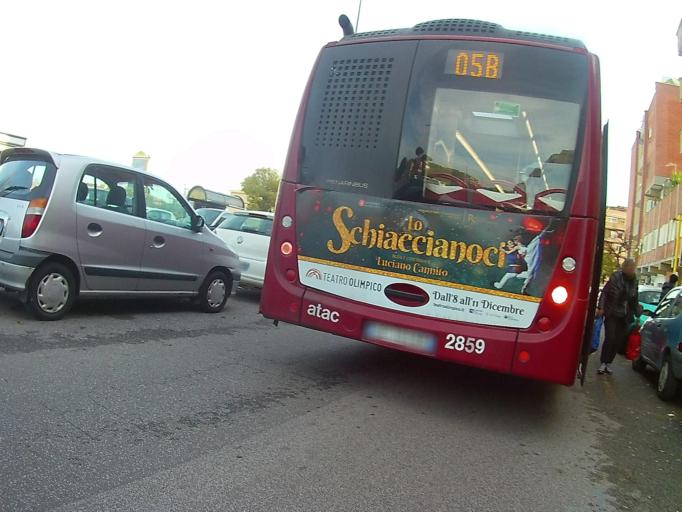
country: IT
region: Latium
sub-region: Citta metropolitana di Roma Capitale
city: Lido di Ostia
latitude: 41.7389
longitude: 12.2875
